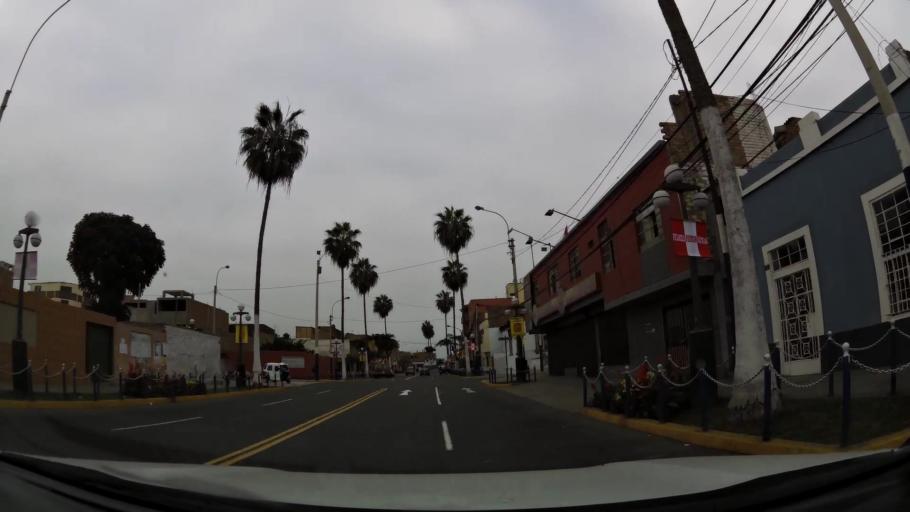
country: PE
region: Lima
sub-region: Lima
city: Surco
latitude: -12.1696
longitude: -77.0287
